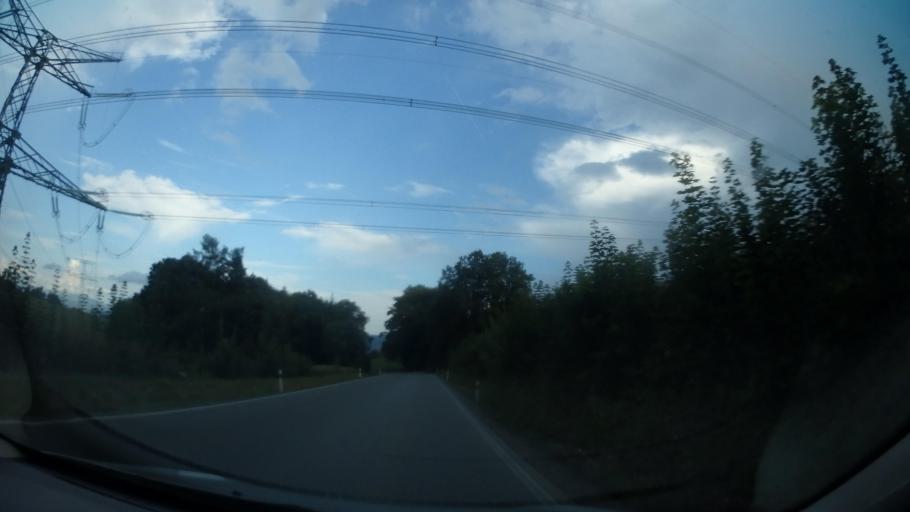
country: CZ
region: Olomoucky
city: Zabreh
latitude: 49.8871
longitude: 16.8445
